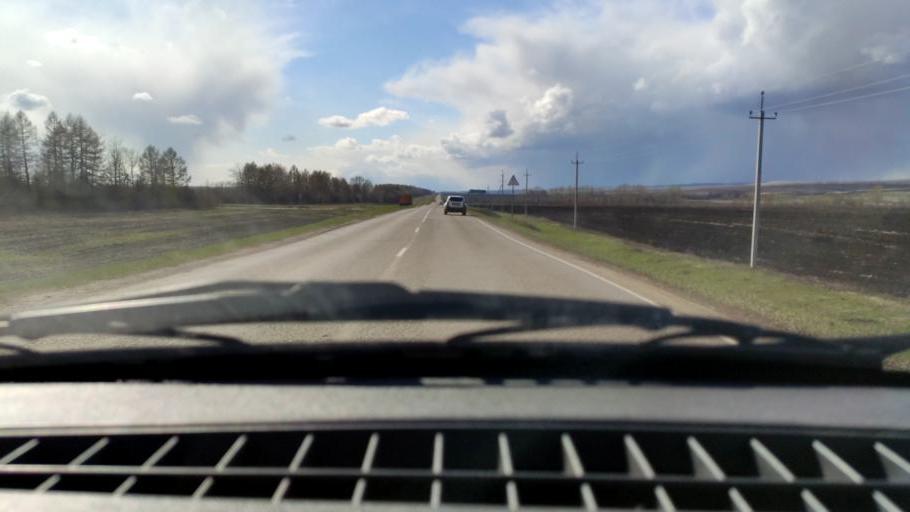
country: RU
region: Bashkortostan
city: Chekmagush
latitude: 55.1091
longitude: 54.9494
